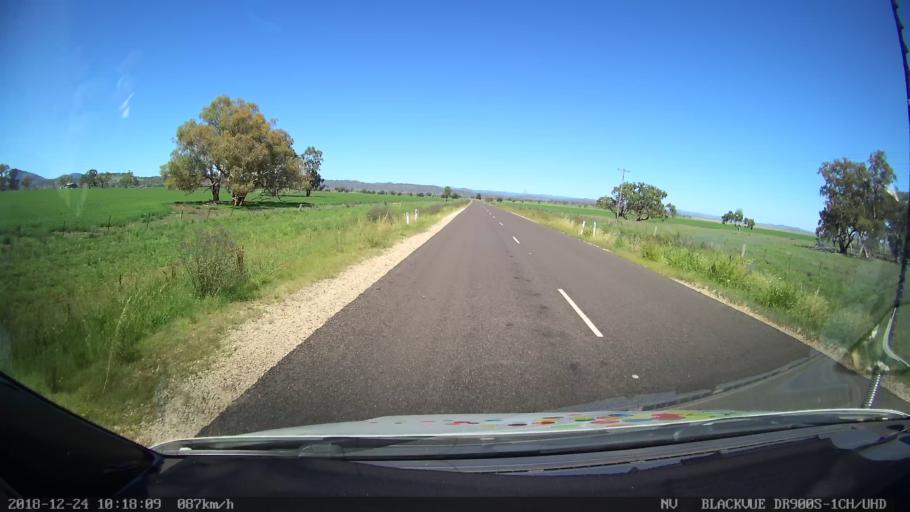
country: AU
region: New South Wales
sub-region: Liverpool Plains
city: Quirindi
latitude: -31.7226
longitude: 150.5808
